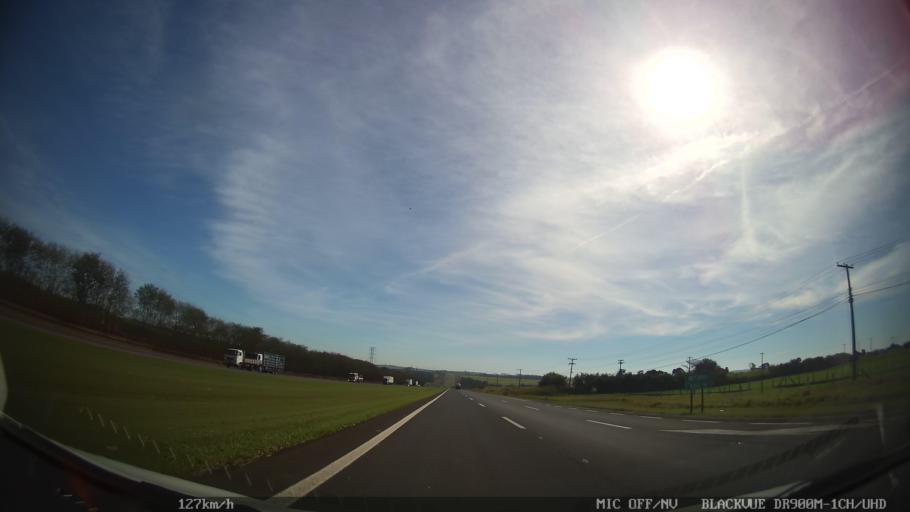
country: BR
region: Sao Paulo
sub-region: Araras
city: Araras
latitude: -22.3204
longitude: -47.3901
